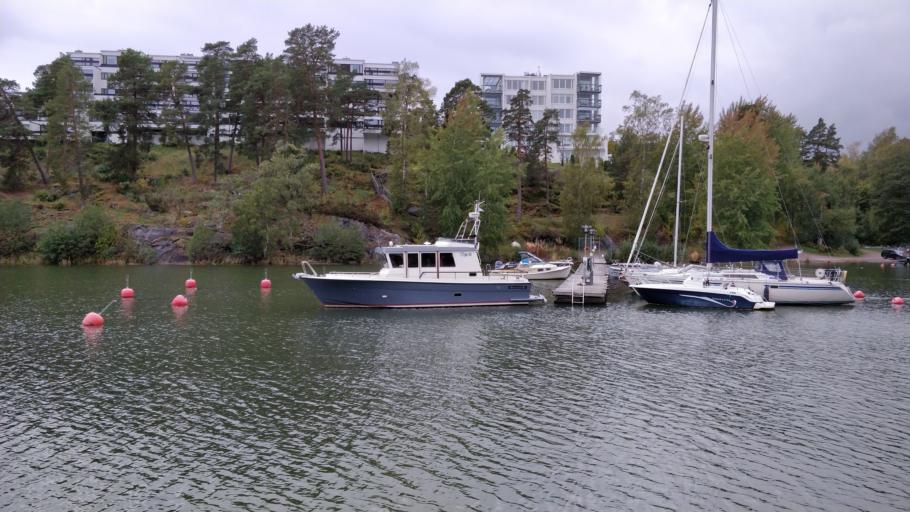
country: FI
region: Uusimaa
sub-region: Helsinki
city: Vantaa
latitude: 60.1828
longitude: 25.0650
